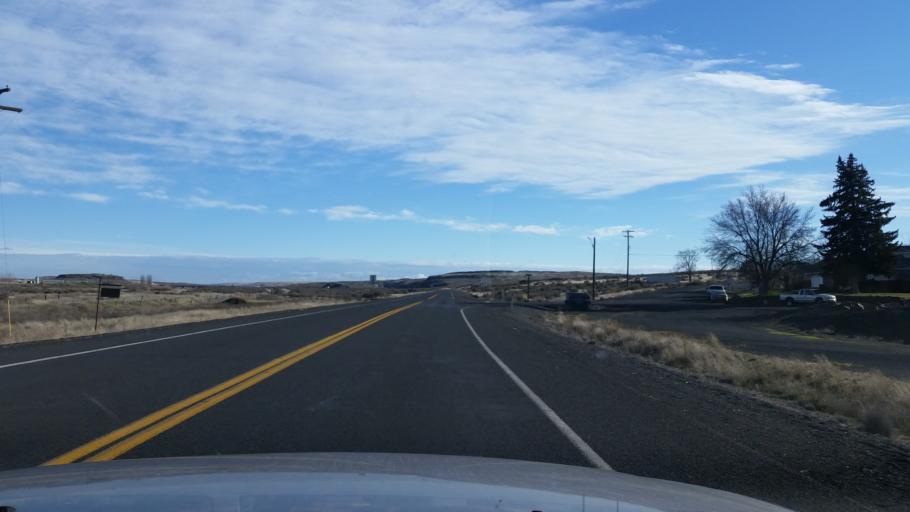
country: US
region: Washington
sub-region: Adams County
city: Ritzville
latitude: 47.3325
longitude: -118.6770
